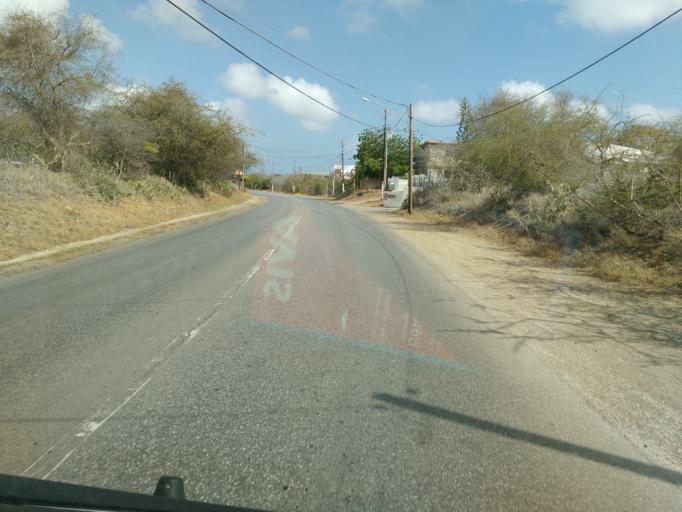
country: CW
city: Willemstad
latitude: 12.0950
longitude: -68.8725
